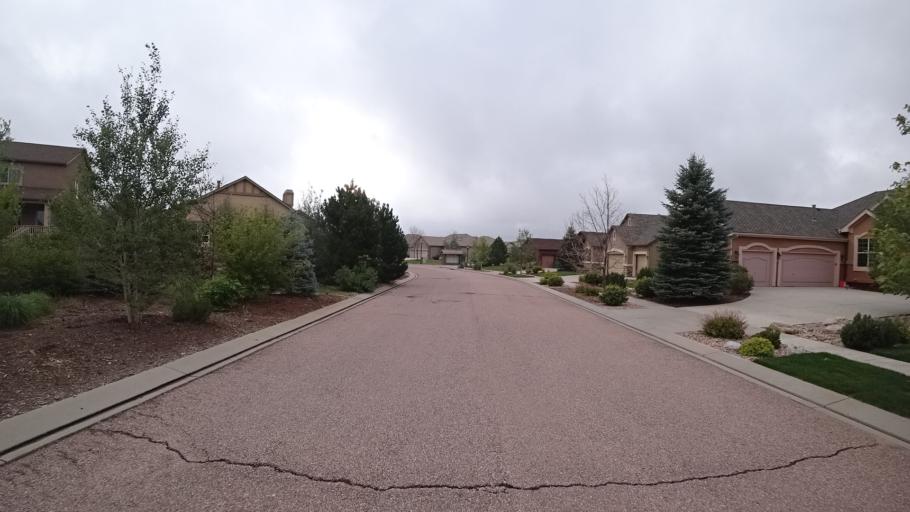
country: US
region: Colorado
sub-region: El Paso County
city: Gleneagle
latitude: 39.0315
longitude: -104.7800
